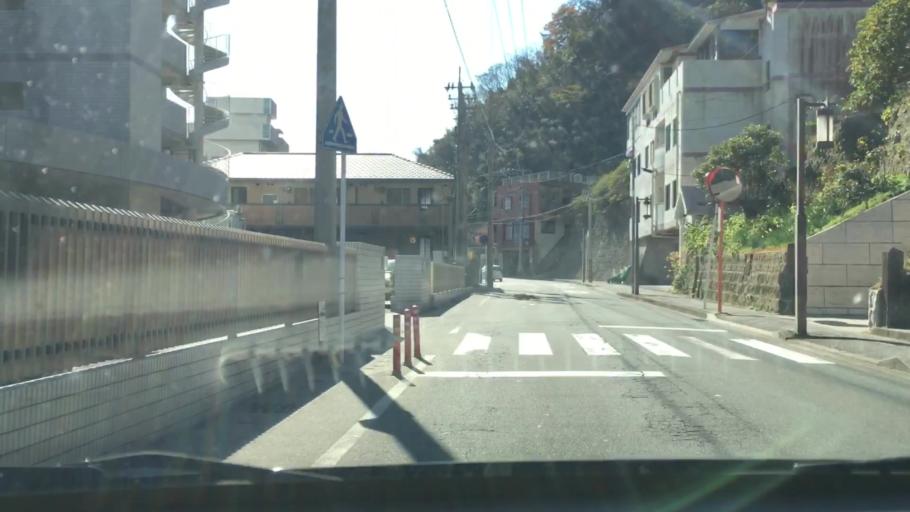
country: JP
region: Kagoshima
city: Kagoshima-shi
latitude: 31.6139
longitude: 130.5746
